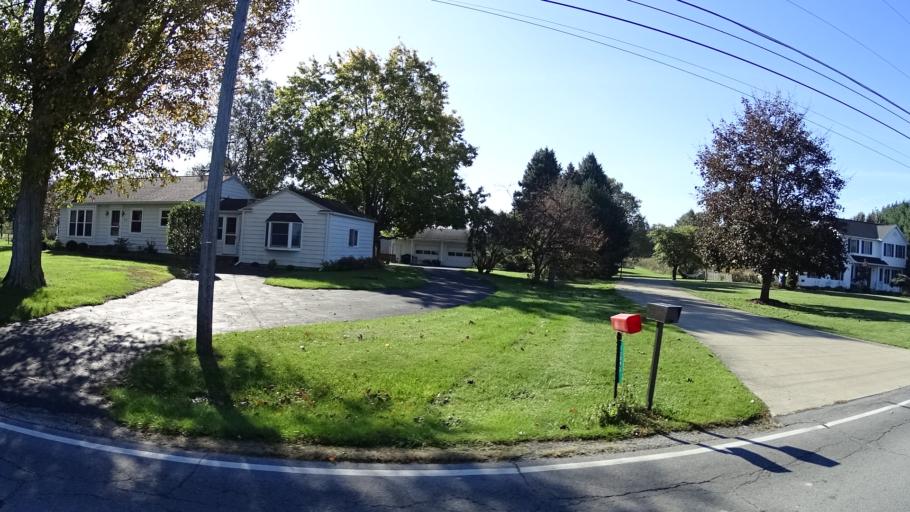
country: US
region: Ohio
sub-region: Lorain County
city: Vermilion-on-the-Lake
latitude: 41.3876
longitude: -82.2979
